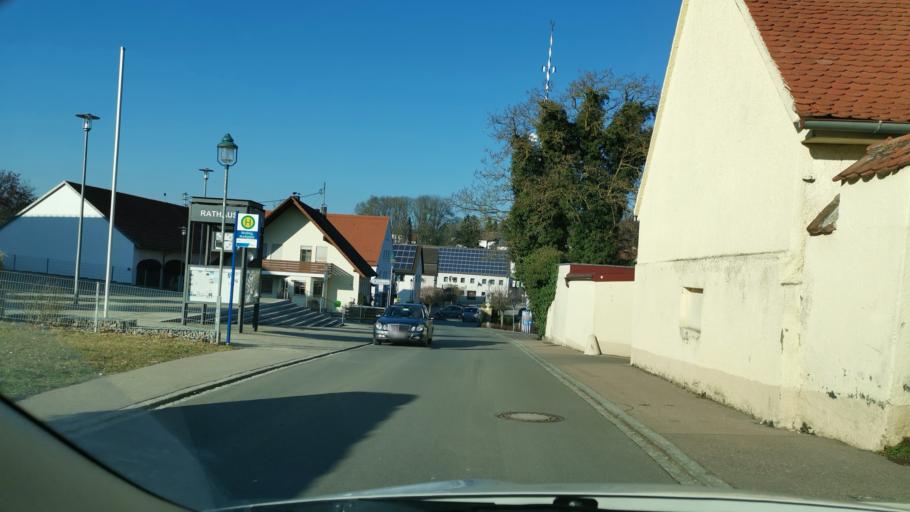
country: DE
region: Bavaria
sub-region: Swabia
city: Aindling
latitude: 48.5118
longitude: 10.9531
